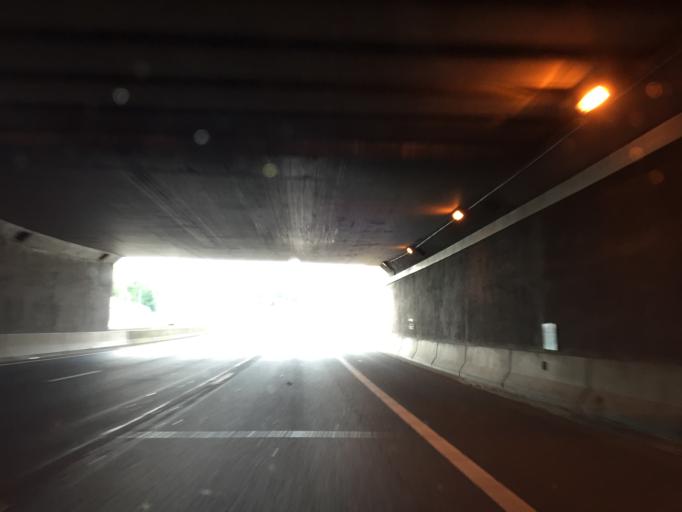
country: NL
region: North Holland
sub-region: Gemeente Amsterdam
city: Amsterdam
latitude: 52.3780
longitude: 4.8444
